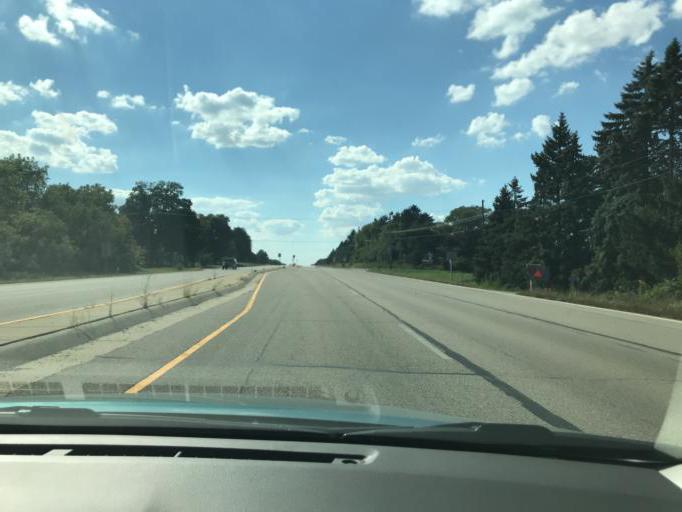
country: US
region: Wisconsin
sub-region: Walworth County
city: Como
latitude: 42.5869
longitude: -88.4803
